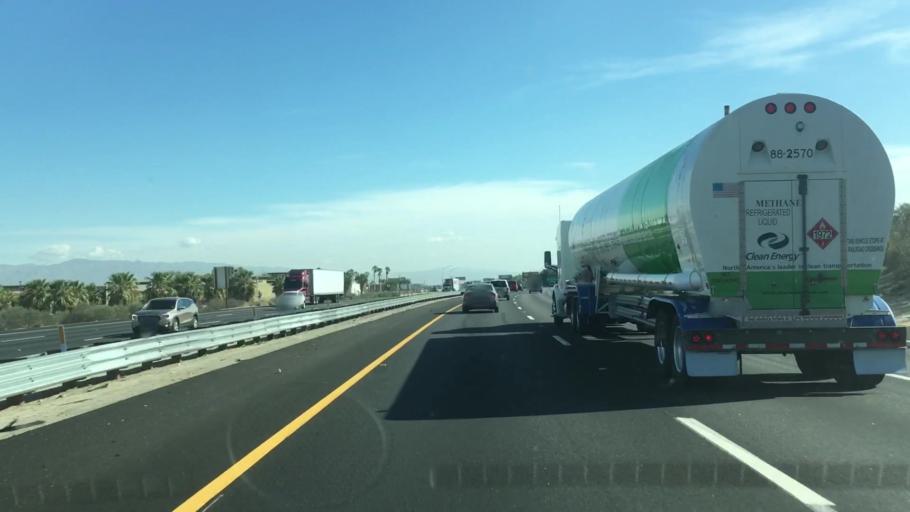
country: US
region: California
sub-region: Riverside County
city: Bermuda Dunes
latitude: 33.7600
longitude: -116.3004
